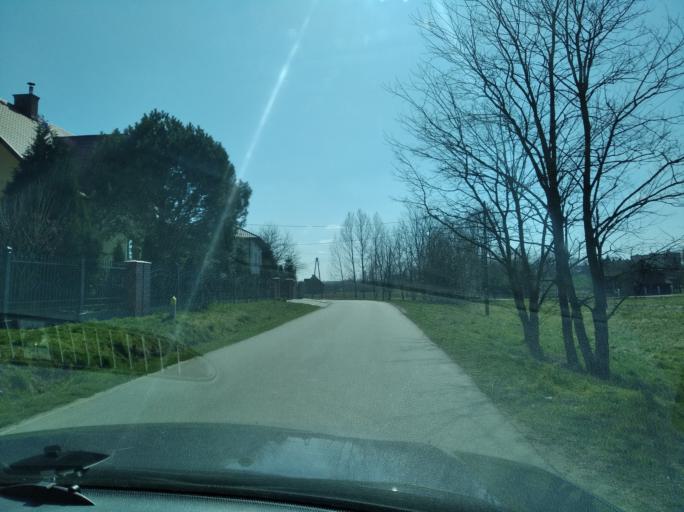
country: PL
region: Subcarpathian Voivodeship
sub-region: Powiat jaroslawski
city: Pawlosiow
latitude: 49.9591
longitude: 22.6513
